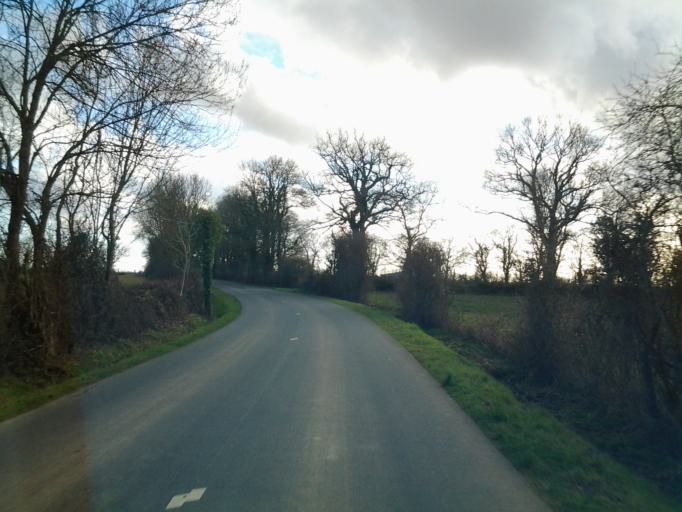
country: FR
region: Pays de la Loire
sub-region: Departement de la Vendee
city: Chateau-Guibert
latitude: 46.6197
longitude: -1.2345
